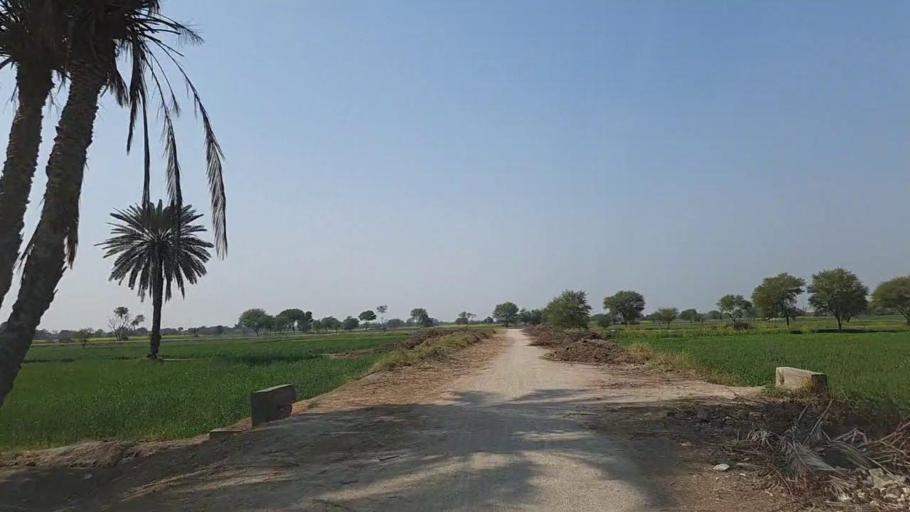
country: PK
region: Sindh
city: Nawabshah
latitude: 26.2532
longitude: 68.4896
